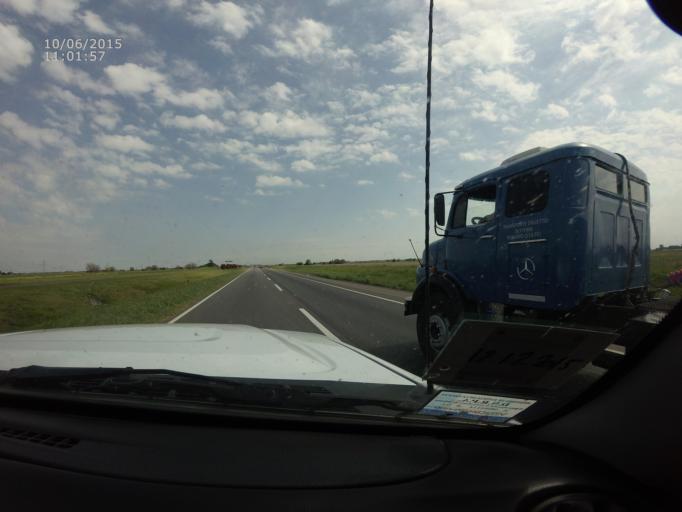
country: AR
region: Santa Fe
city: Villa Constitucion
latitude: -33.2537
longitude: -60.4237
